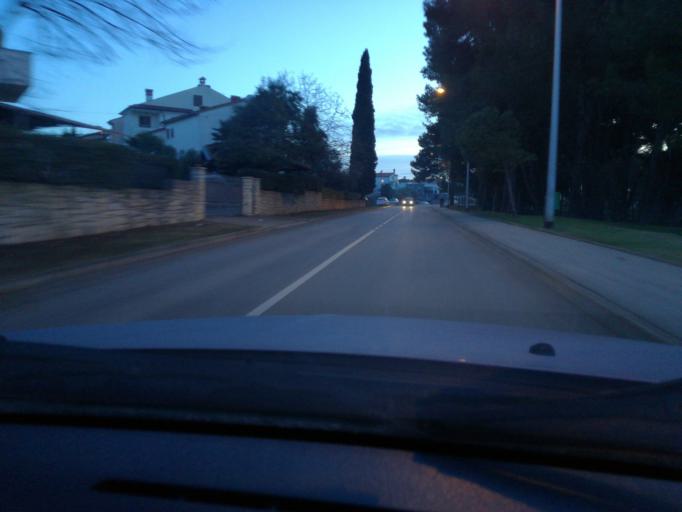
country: HR
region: Istarska
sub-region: Grad Rovinj
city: Rovinj
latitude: 45.0864
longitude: 13.6453
